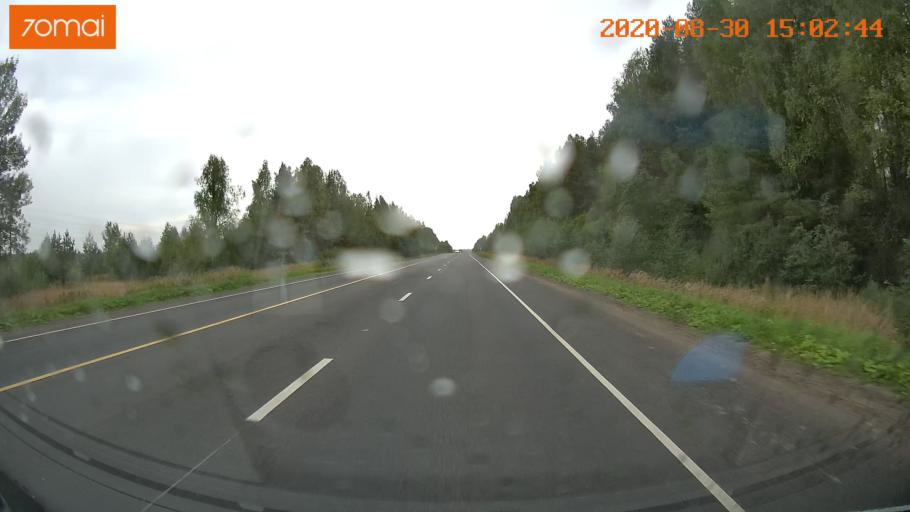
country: RU
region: Ivanovo
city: Staraya Vichuga
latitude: 57.3075
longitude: 41.9205
